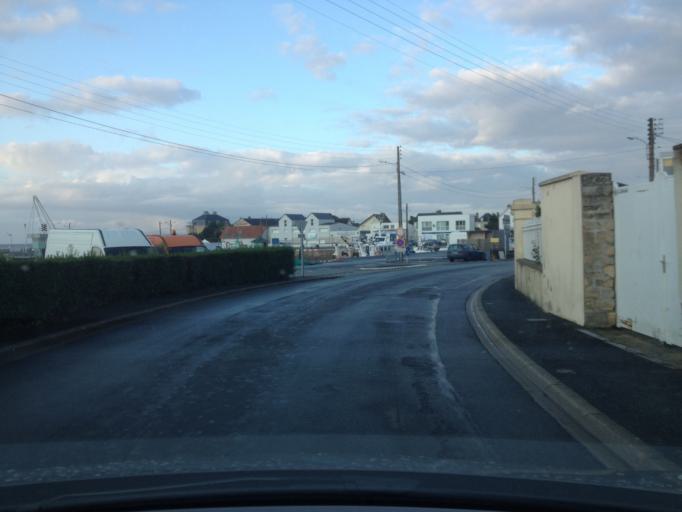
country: FR
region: Lower Normandy
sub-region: Departement du Calvados
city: Grandcamp-Maisy
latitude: 49.3874
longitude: -1.0486
